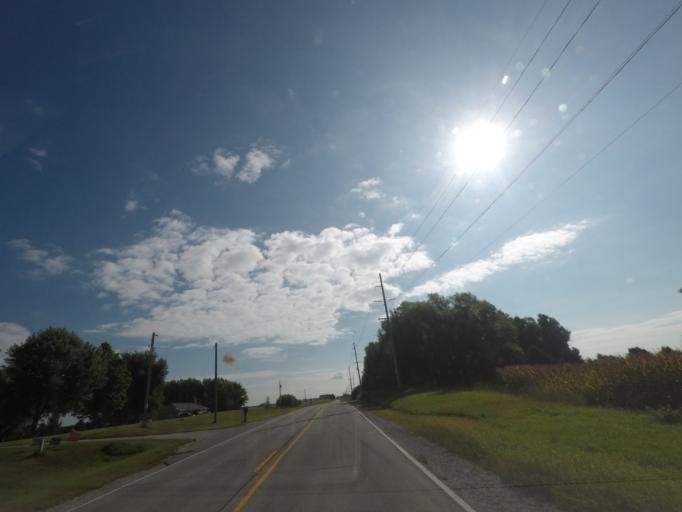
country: US
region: Iowa
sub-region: Story County
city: Nevada
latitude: 42.0227
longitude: -93.4194
